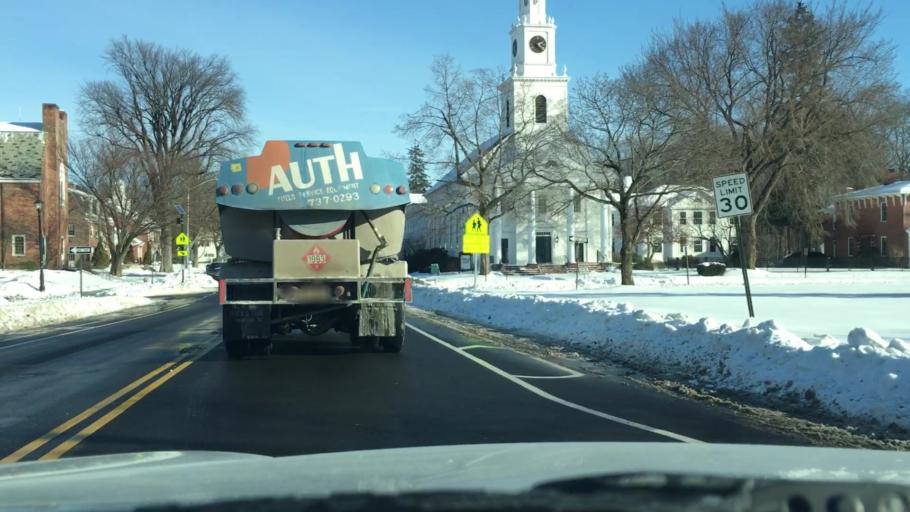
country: US
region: Massachusetts
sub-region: Hampden County
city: Longmeadow
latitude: 42.0505
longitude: -72.5827
